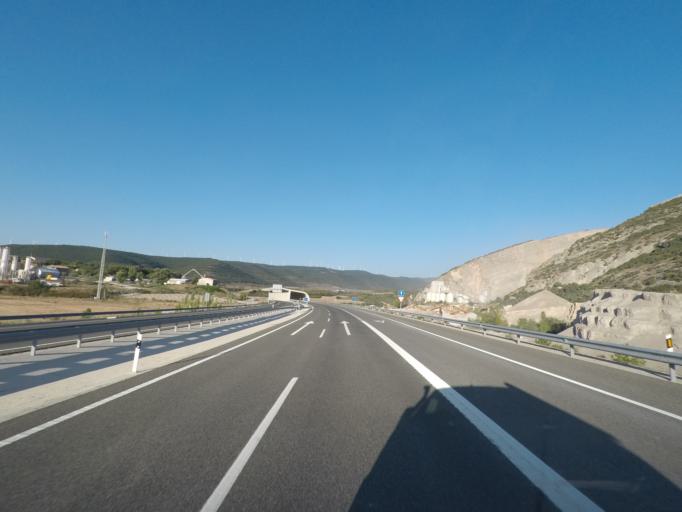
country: ES
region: Navarre
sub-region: Provincia de Navarra
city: Liedena
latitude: 42.6234
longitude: -1.2753
